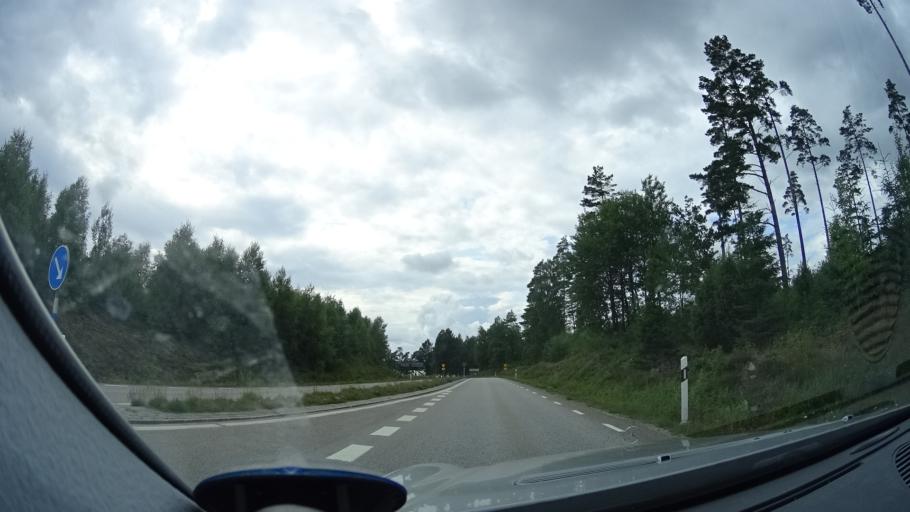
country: SE
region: Kronoberg
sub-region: Tingsryds Kommun
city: Tingsryd
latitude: 56.5147
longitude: 14.9949
